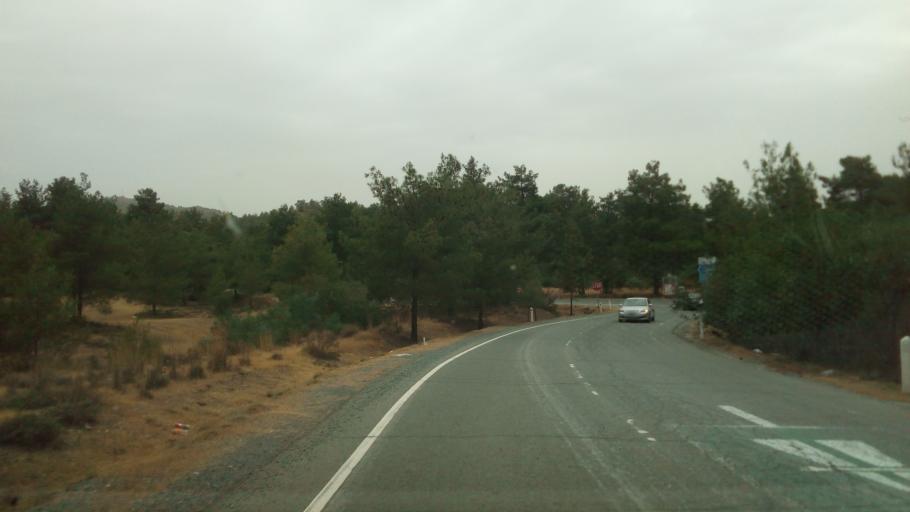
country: CY
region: Larnaka
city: Kornos
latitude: 34.9263
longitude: 33.4072
